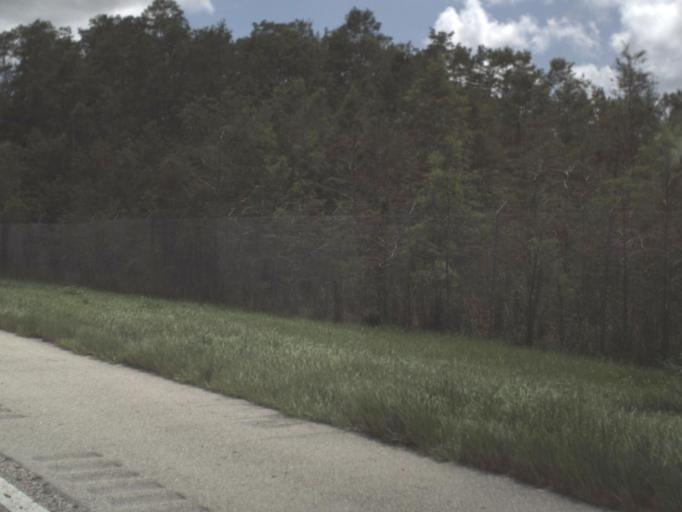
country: US
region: Florida
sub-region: Collier County
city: Immokalee
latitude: 26.1691
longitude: -81.0387
